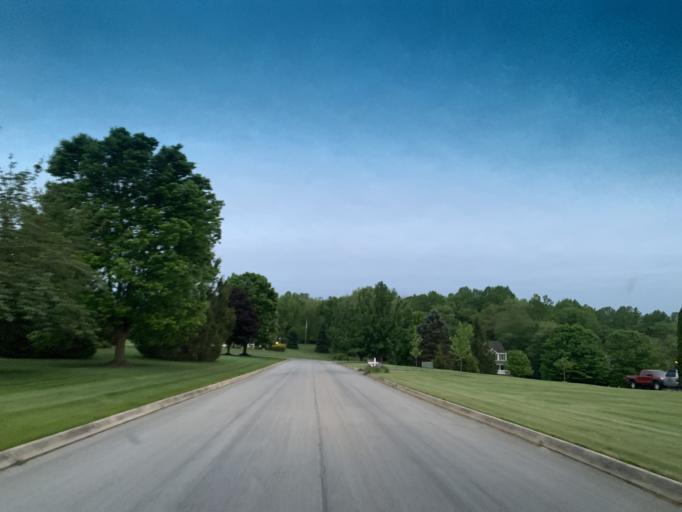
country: US
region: Maryland
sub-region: Harford County
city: South Bel Air
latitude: 39.5902
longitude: -76.2657
